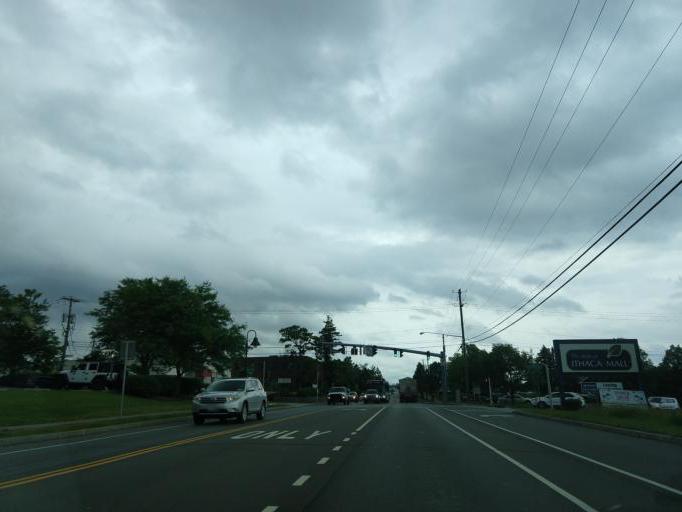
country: US
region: New York
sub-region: Tompkins County
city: Lansing
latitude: 42.4865
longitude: -76.4876
